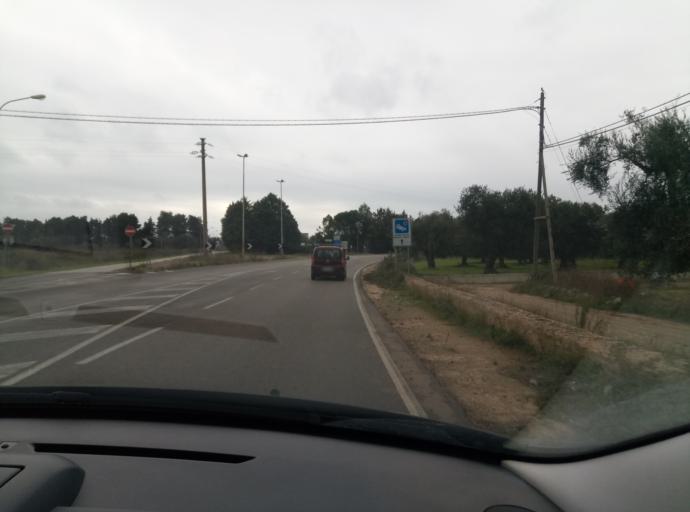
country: IT
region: Apulia
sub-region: Provincia di Bari
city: Acquaviva delle Fonti
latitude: 40.9091
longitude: 16.8510
